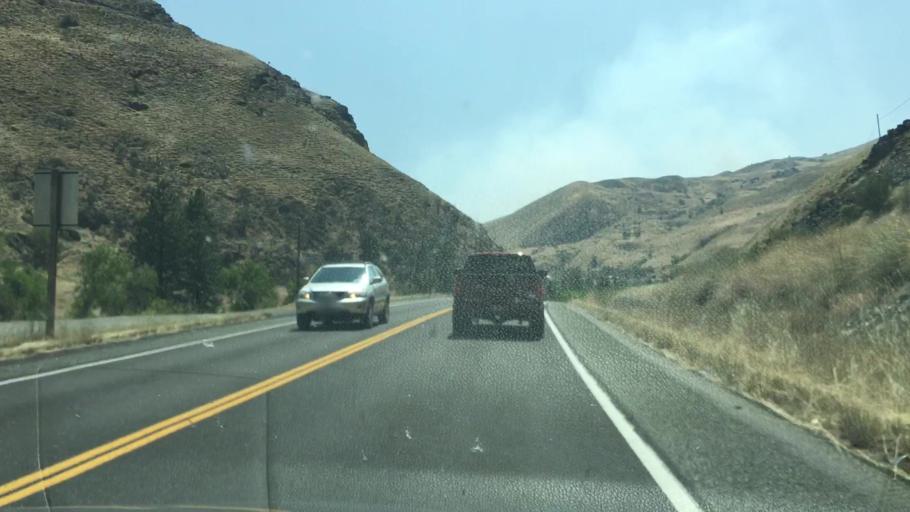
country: US
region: Idaho
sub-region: Valley County
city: McCall
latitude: 45.3638
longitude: -116.3598
